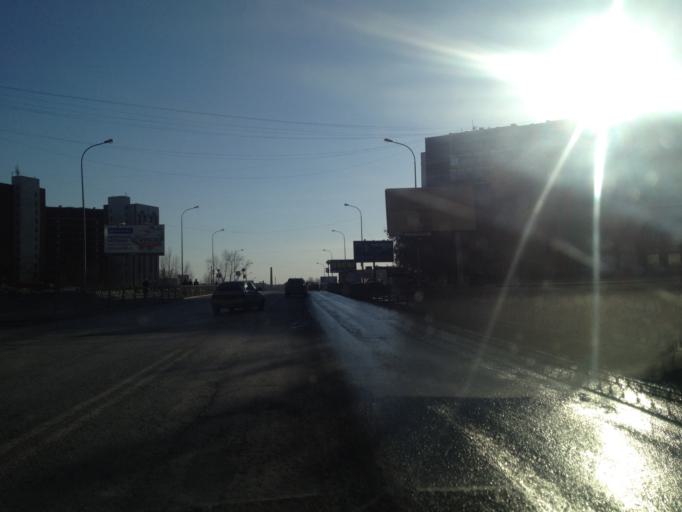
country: RU
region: Sverdlovsk
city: Yekaterinburg
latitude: 56.8507
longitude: 60.5688
